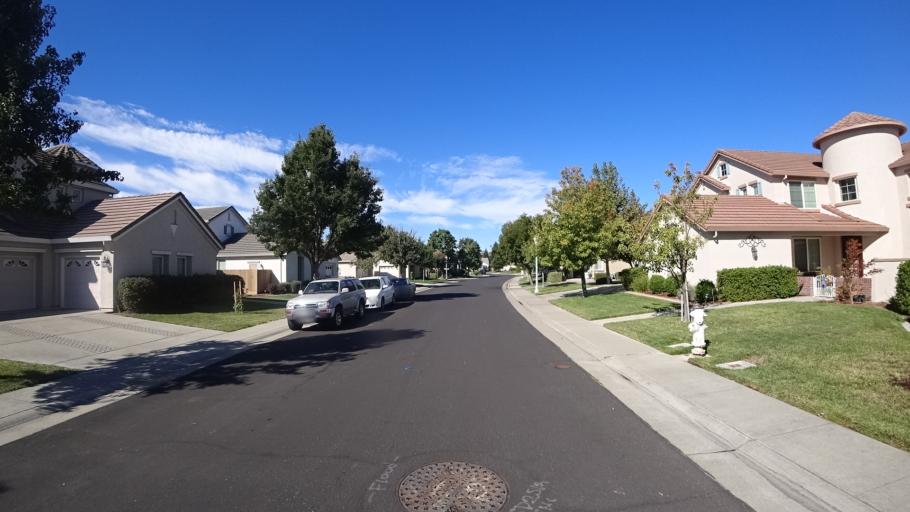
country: US
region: California
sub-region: Sacramento County
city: Laguna
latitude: 38.4236
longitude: -121.4782
